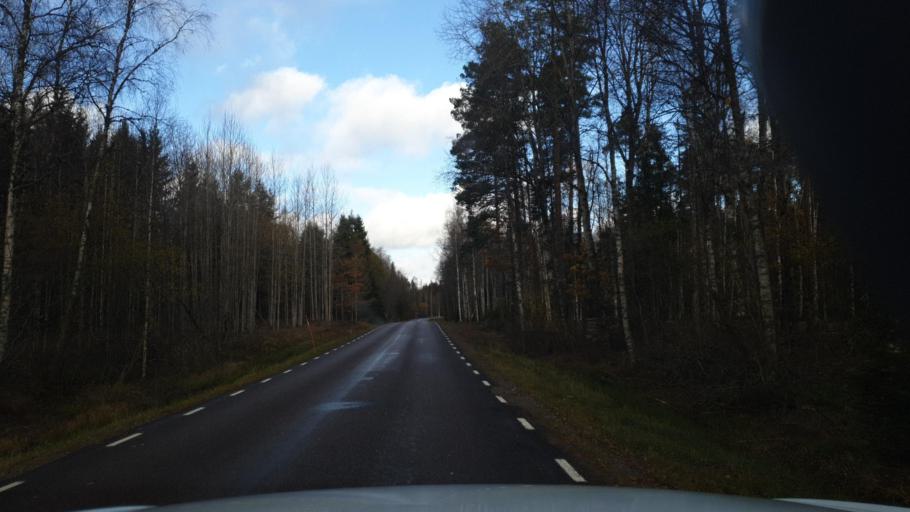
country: SE
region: Vaermland
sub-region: Grums Kommun
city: Slottsbron
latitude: 59.4827
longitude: 12.8832
